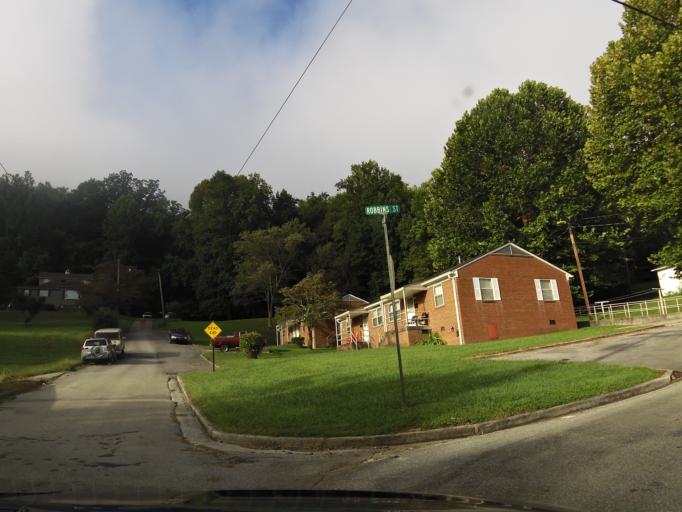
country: US
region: Tennessee
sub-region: Campbell County
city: Jellico
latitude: 36.5846
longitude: -84.1225
